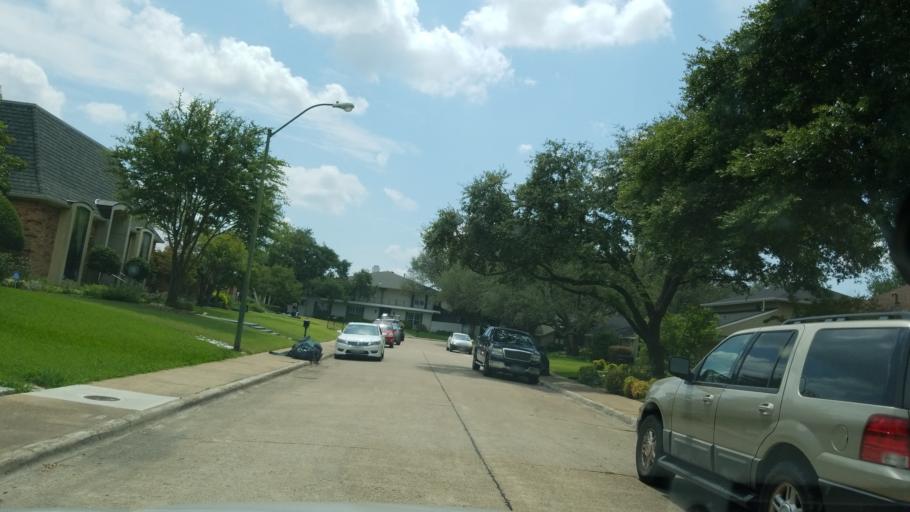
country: US
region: Texas
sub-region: Dallas County
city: Richardson
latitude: 32.8921
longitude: -96.7204
